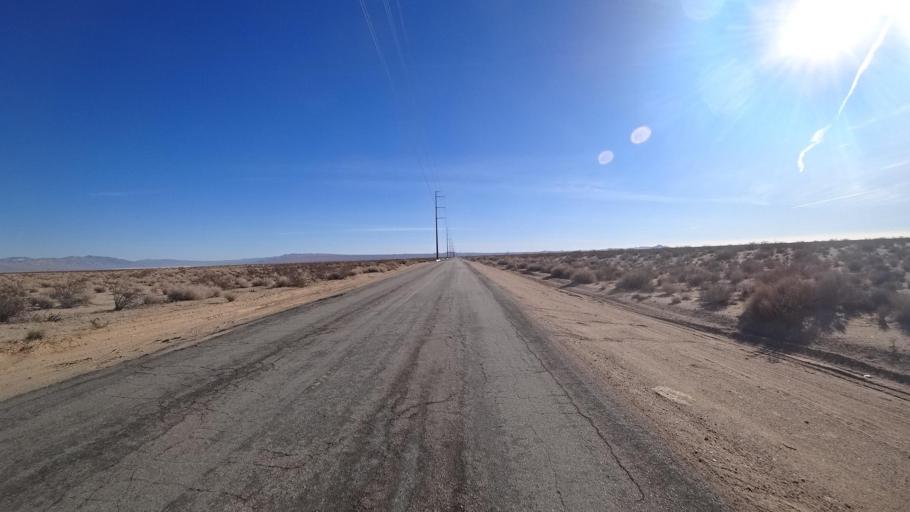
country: US
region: California
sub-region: Kern County
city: California City
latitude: 35.1985
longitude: -118.0518
